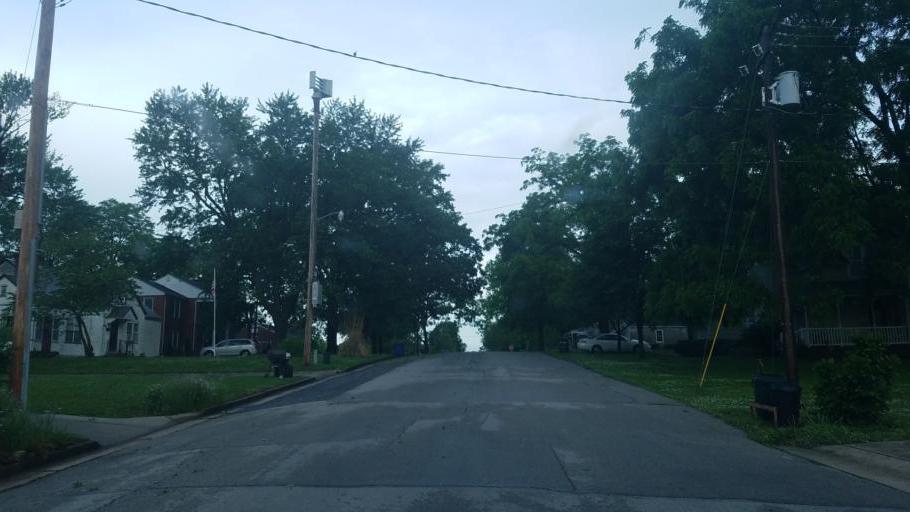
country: US
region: Missouri
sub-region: Moniteau County
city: California
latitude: 38.6242
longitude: -92.5678
